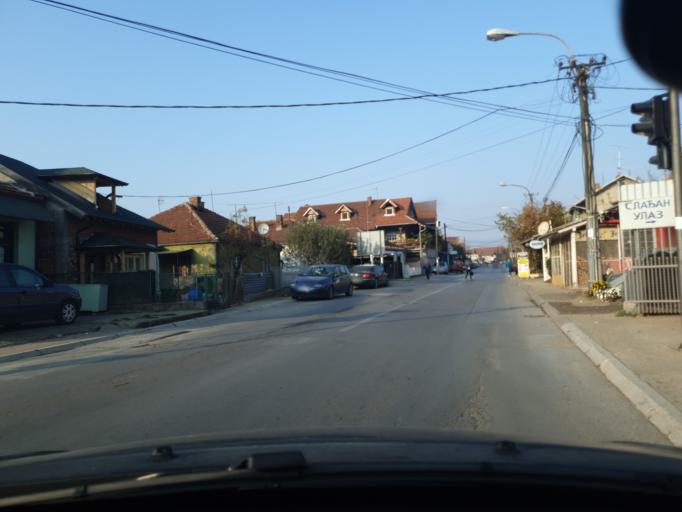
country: RS
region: Central Serbia
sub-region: Jablanicki Okrug
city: Leskovac
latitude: 42.9944
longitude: 21.9342
